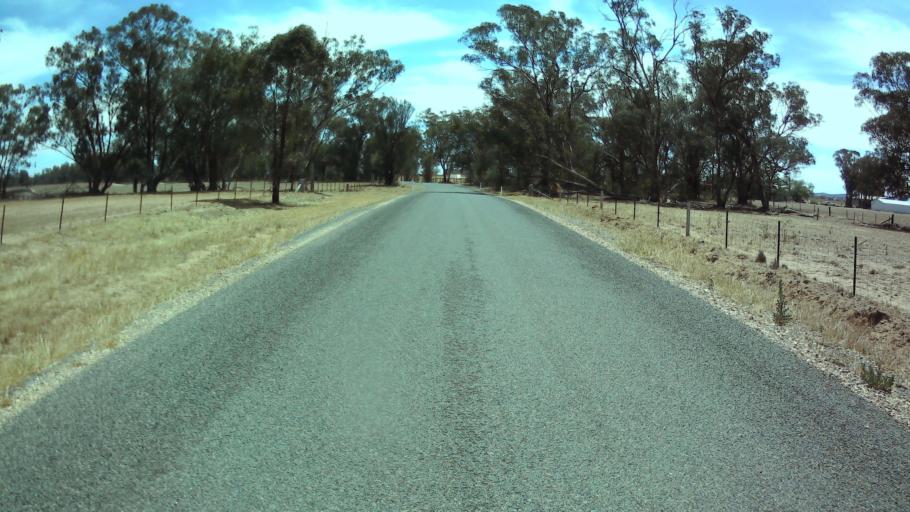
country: AU
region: New South Wales
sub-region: Weddin
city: Grenfell
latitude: -33.7396
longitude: 148.2089
